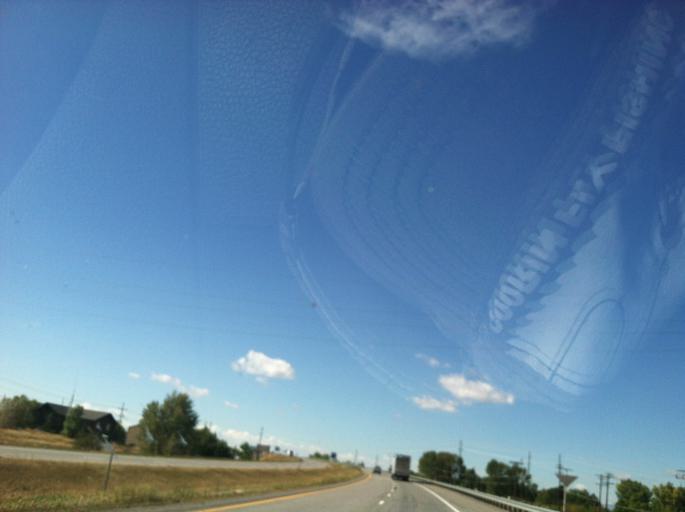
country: US
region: Montana
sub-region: Gallatin County
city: Bozeman
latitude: 45.6906
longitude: -111.0220
